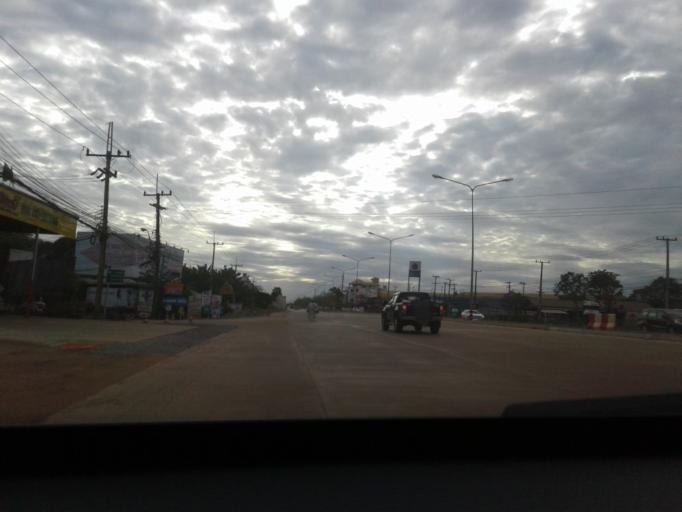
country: TH
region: Changwat Udon Thani
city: Udon Thani
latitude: 17.4306
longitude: 102.7846
